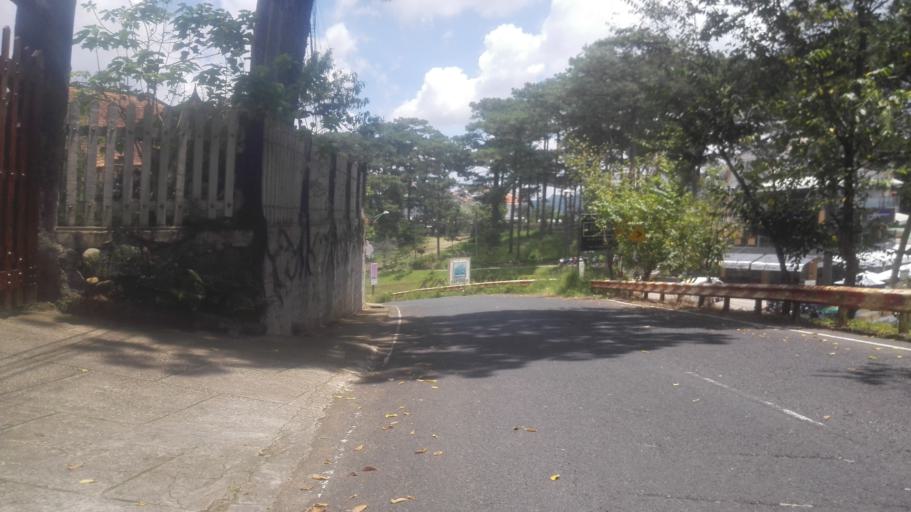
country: VN
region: Lam Dong
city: Da Lat
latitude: 11.9246
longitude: 108.4464
